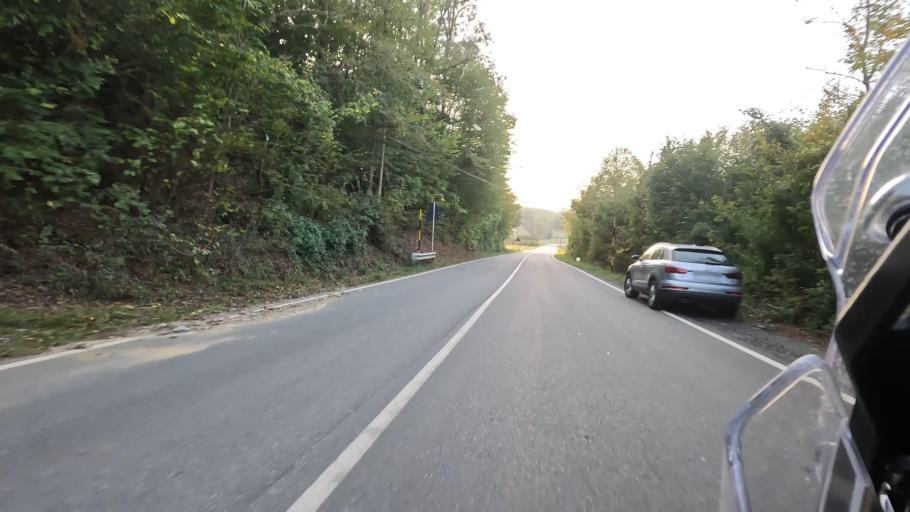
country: IT
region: Liguria
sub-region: Provincia di Savona
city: Sassello
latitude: 44.5095
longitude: 8.4792
